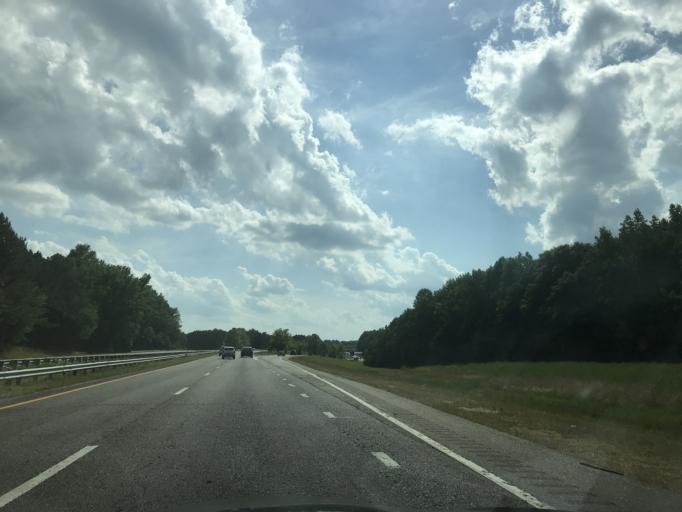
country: US
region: North Carolina
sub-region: Nash County
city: Nashville
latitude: 35.9755
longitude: -77.9323
